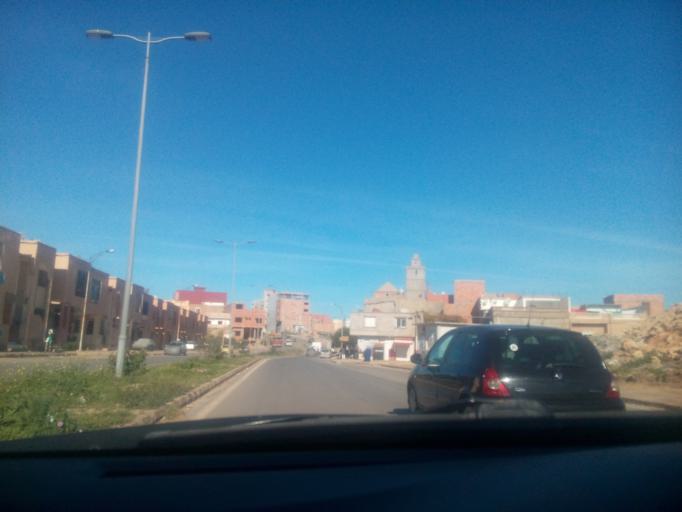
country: DZ
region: Oran
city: Bir el Djir
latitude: 35.7475
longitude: -0.5500
